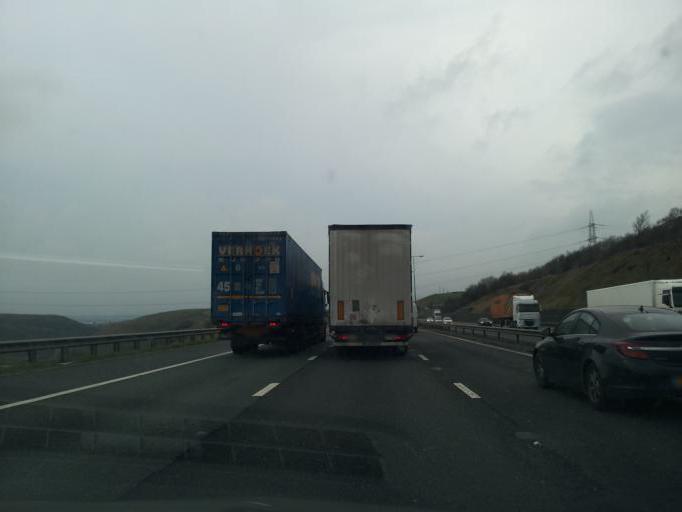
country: GB
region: England
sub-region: Borough of Rochdale
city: Littleborough
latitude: 53.6243
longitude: -2.0646
